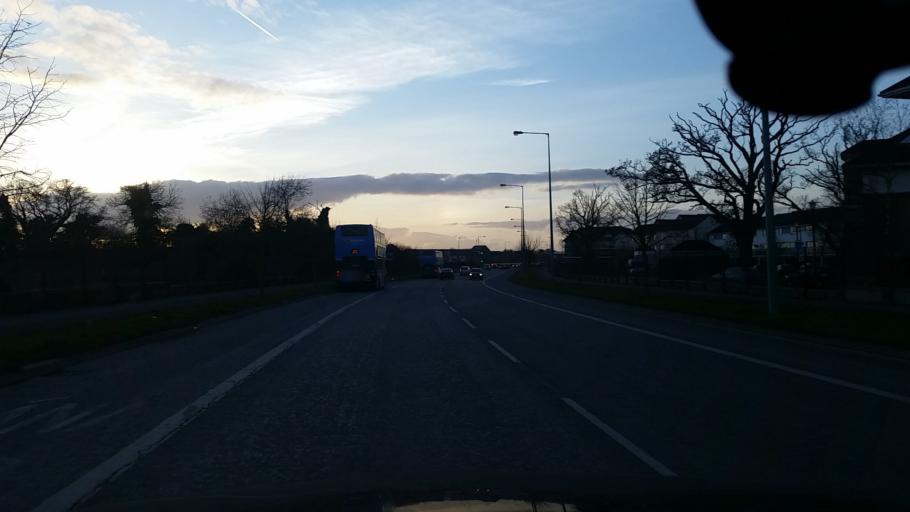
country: IE
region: Leinster
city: Hartstown
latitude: 53.3913
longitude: -6.4348
